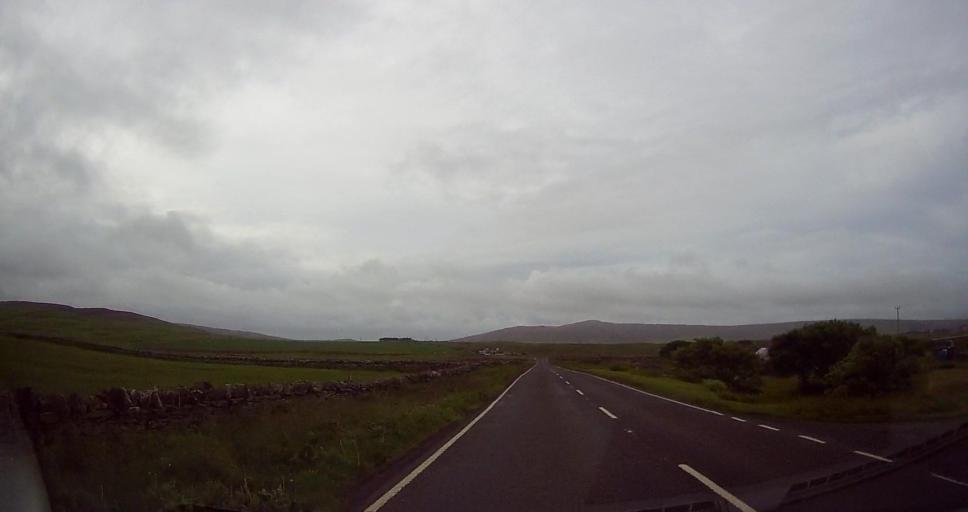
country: GB
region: Scotland
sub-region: Orkney Islands
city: Stromness
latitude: 59.0104
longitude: -3.1552
